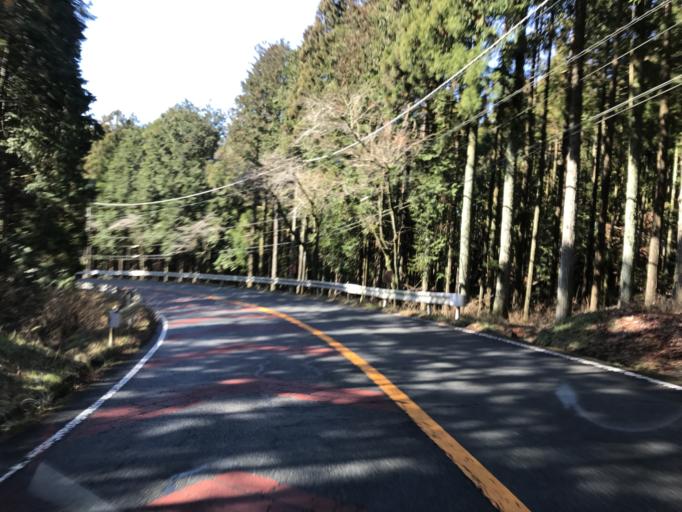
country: JP
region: Shizuoka
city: Fujinomiya
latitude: 35.2909
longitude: 138.6620
